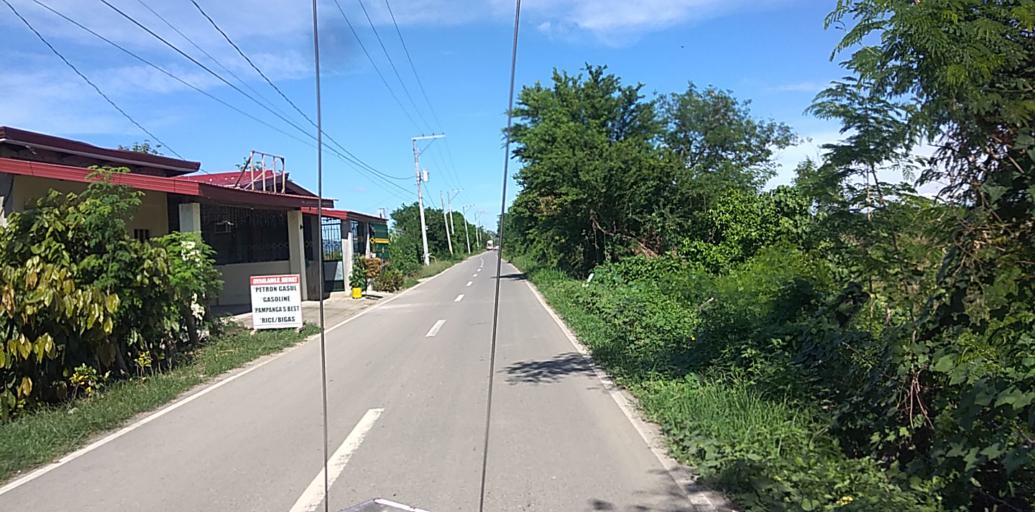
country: PH
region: Central Luzon
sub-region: Province of Pampanga
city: Candaba
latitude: 15.1158
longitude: 120.8148
